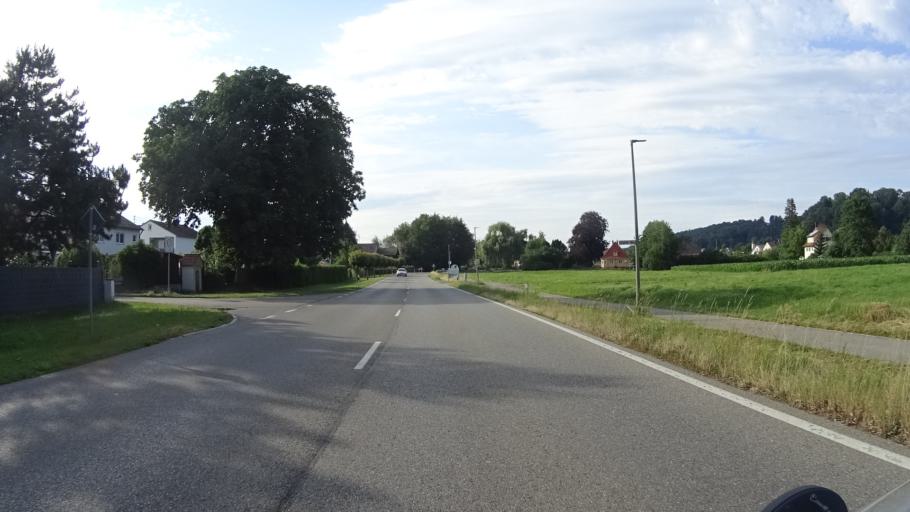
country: DE
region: Bavaria
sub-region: Swabia
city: Altenstadt
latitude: 48.1544
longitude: 10.1151
